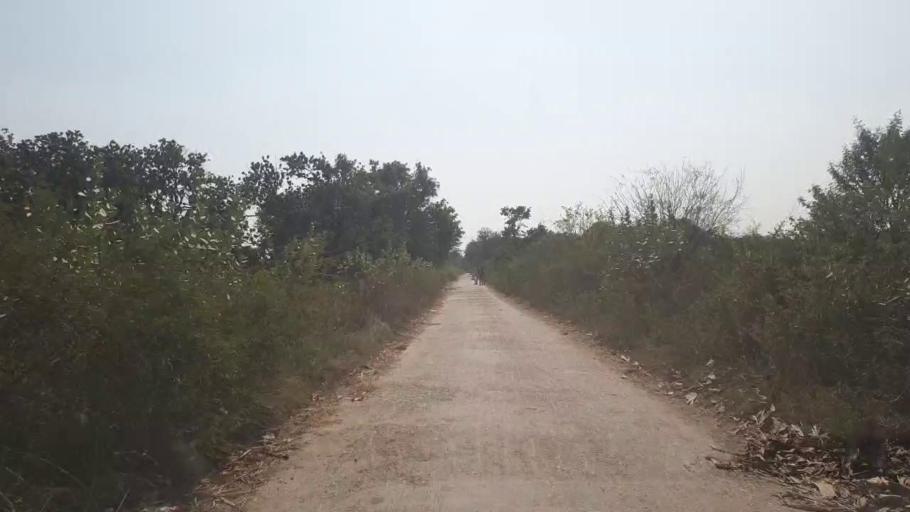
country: PK
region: Sindh
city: Tando Allahyar
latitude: 25.4854
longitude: 68.8481
